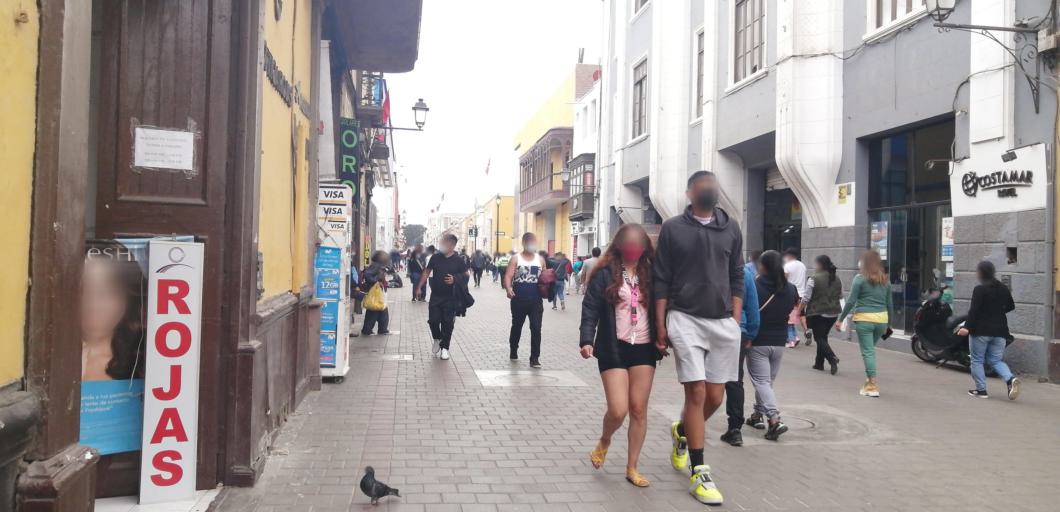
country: PE
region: La Libertad
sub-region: Provincia de Trujillo
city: Trujillo
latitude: -8.1111
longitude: -79.0271
